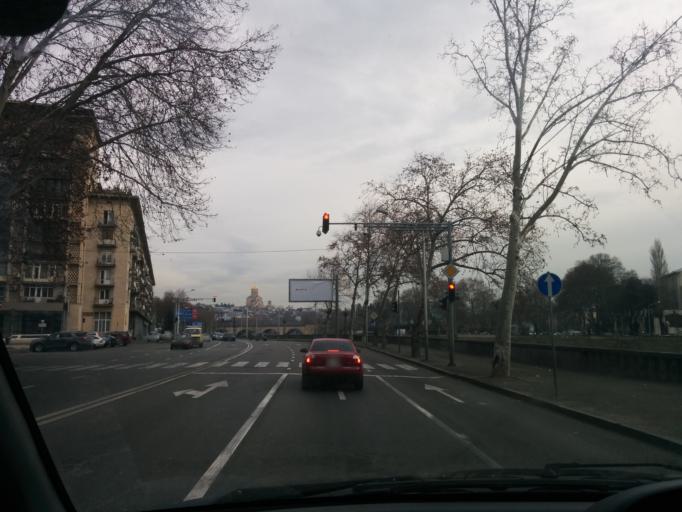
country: GE
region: T'bilisi
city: Tbilisi
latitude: 41.7042
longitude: 44.7980
